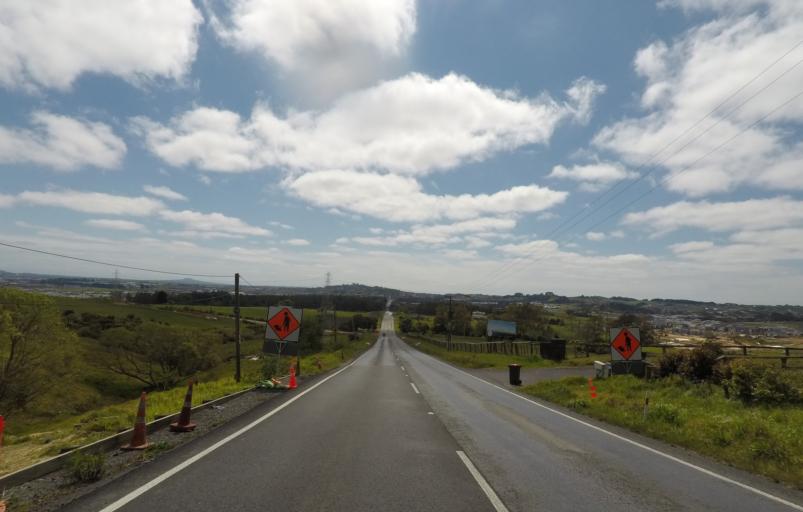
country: NZ
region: Auckland
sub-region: Auckland
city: Manukau City
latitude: -36.9884
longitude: 174.9187
